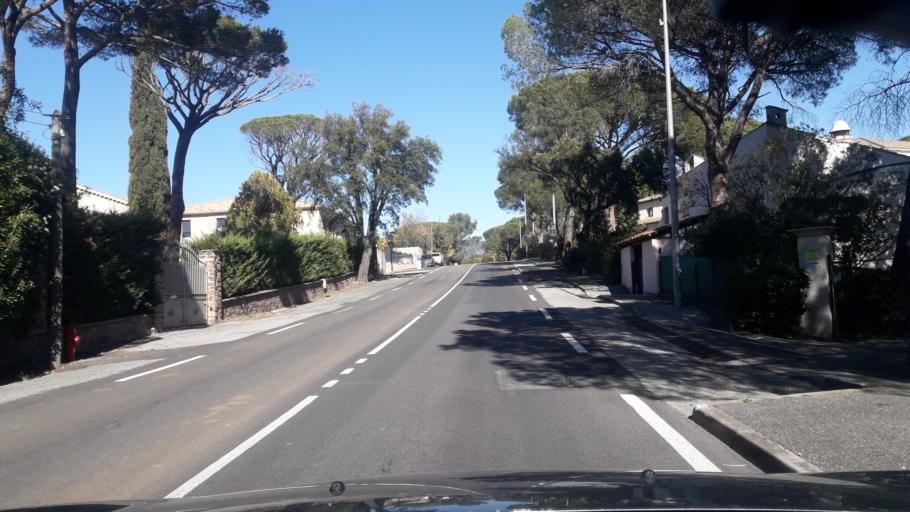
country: FR
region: Provence-Alpes-Cote d'Azur
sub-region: Departement du Var
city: Saint-Raphael
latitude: 43.4496
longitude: 6.7794
